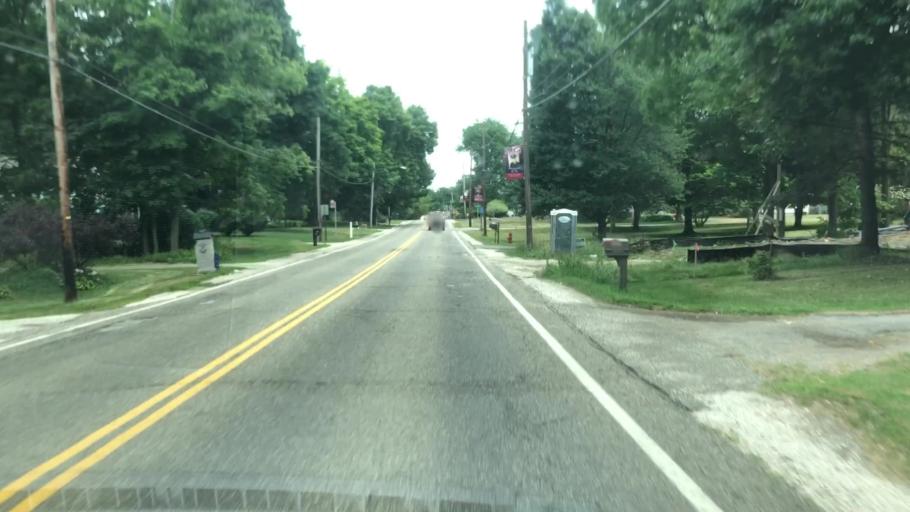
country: US
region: Ohio
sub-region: Summit County
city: Munroe Falls
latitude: 41.1399
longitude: -81.4447
